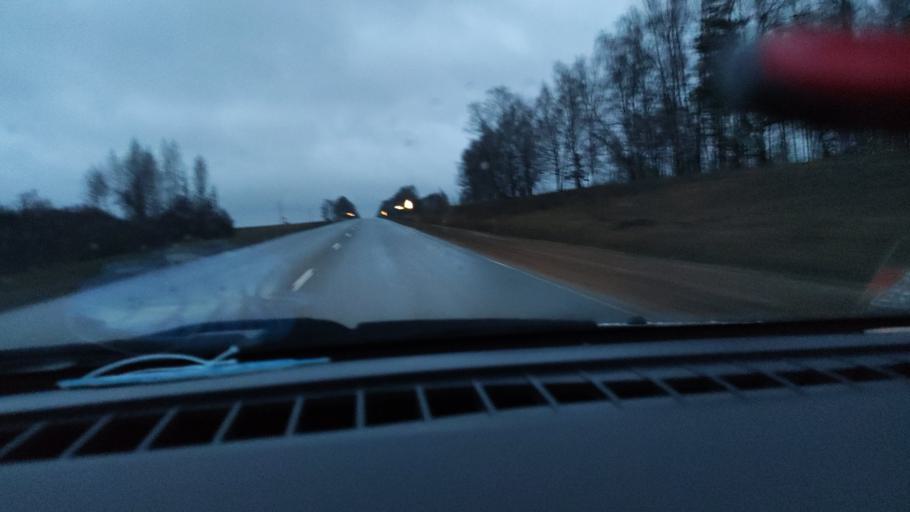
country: RU
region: Udmurtiya
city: Mozhga
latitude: 56.3174
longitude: 52.3260
